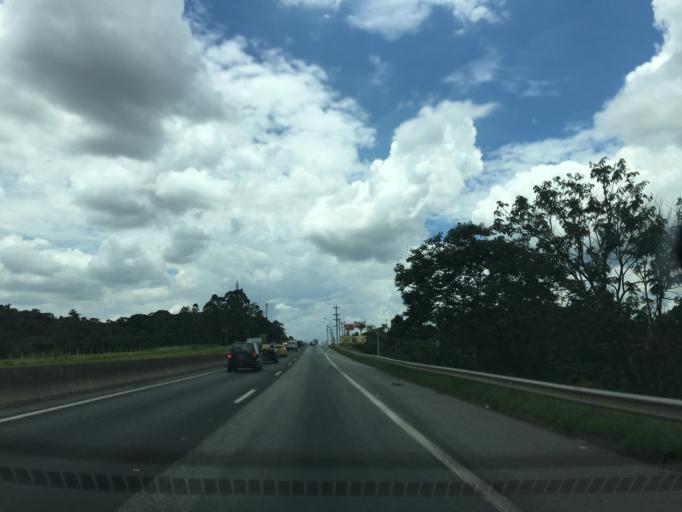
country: BR
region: Sao Paulo
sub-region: Atibaia
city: Atibaia
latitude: -23.2120
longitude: -46.5930
